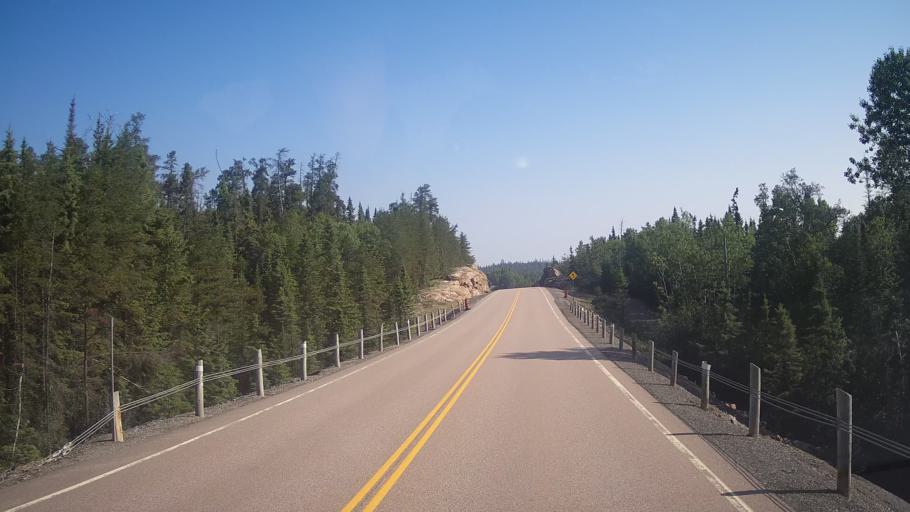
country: CA
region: Ontario
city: Rayside-Balfour
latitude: 46.9858
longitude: -81.6339
